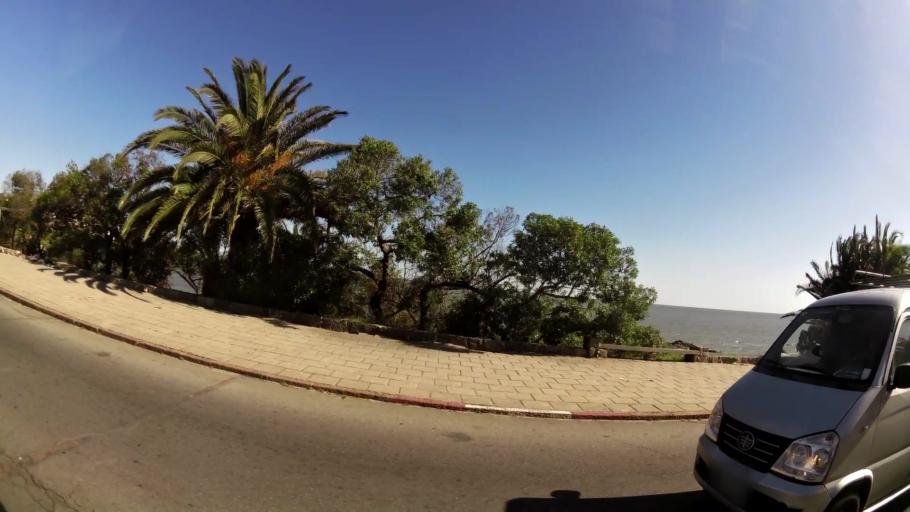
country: UY
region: Canelones
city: Paso de Carrasco
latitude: -34.8954
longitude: -56.0865
